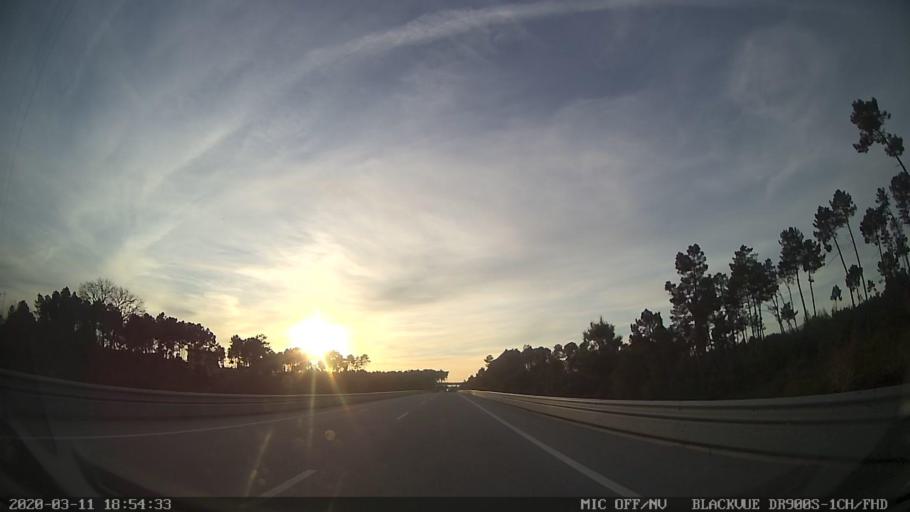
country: PT
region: Vila Real
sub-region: Vila Real
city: Vila Real
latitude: 41.2714
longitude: -7.6864
